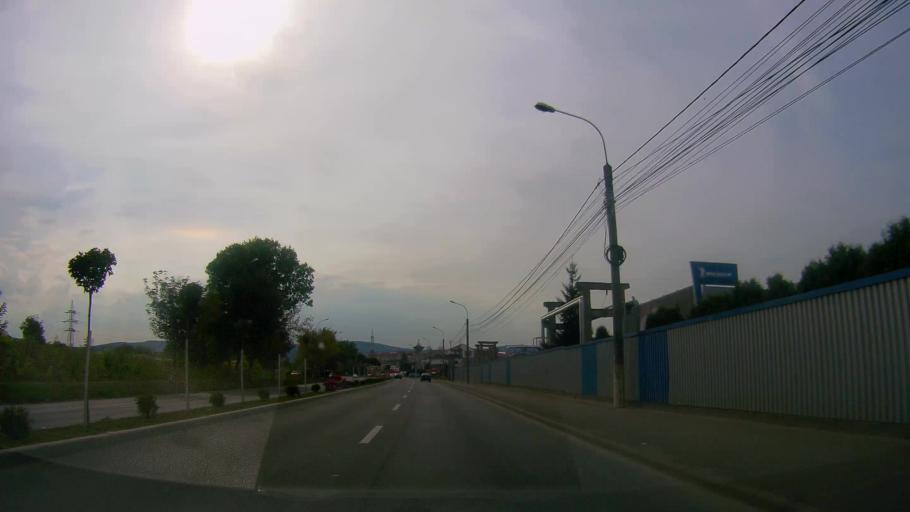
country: RO
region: Salaj
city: Zalau
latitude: 47.2079
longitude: 23.0453
